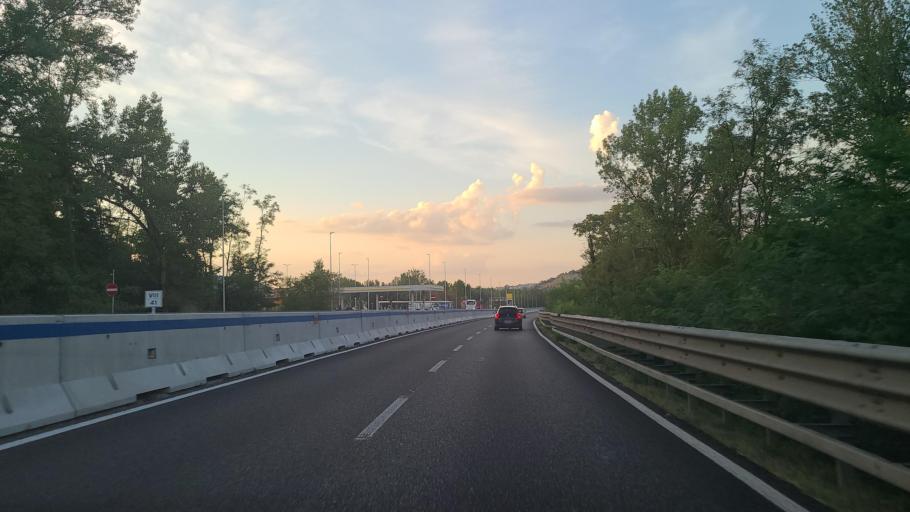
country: IT
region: Tuscany
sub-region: Province of Florence
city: Sambuca
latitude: 43.6049
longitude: 11.1916
